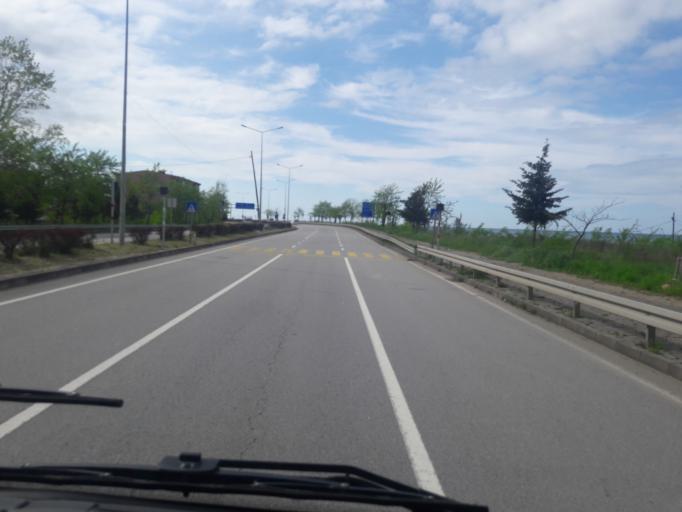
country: TR
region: Giresun
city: Piraziz
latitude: 40.9560
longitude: 38.1195
